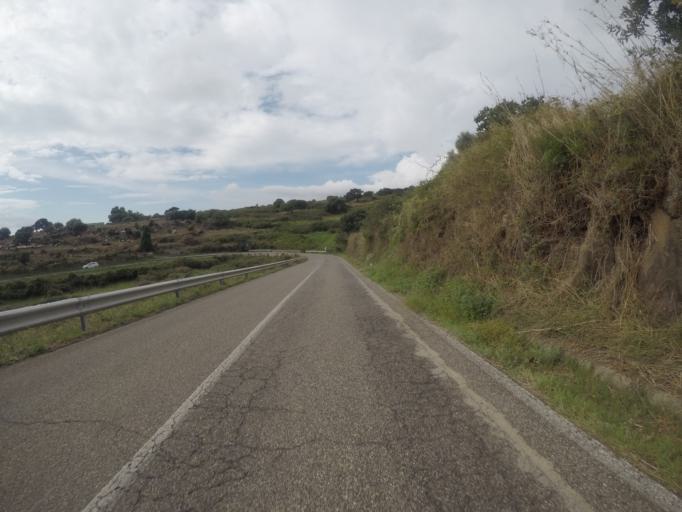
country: IT
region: Sardinia
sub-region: Provincia di Oristano
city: Bonarcado
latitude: 40.1163
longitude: 8.6522
